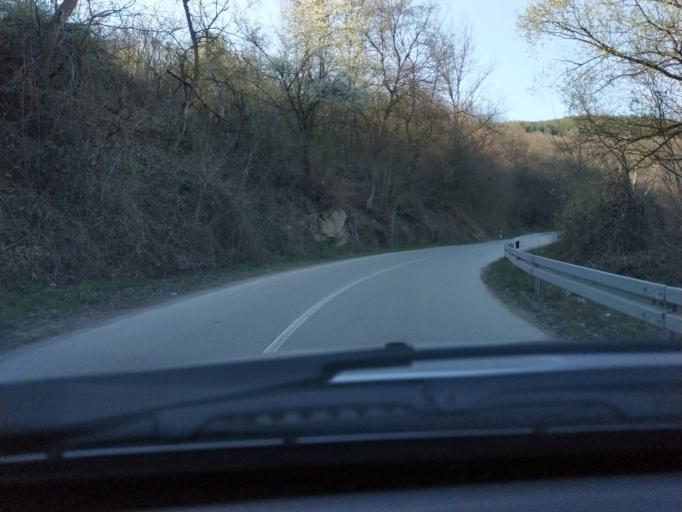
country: RS
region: Central Serbia
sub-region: Nisavski Okrug
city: Aleksinac
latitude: 43.5371
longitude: 21.8040
